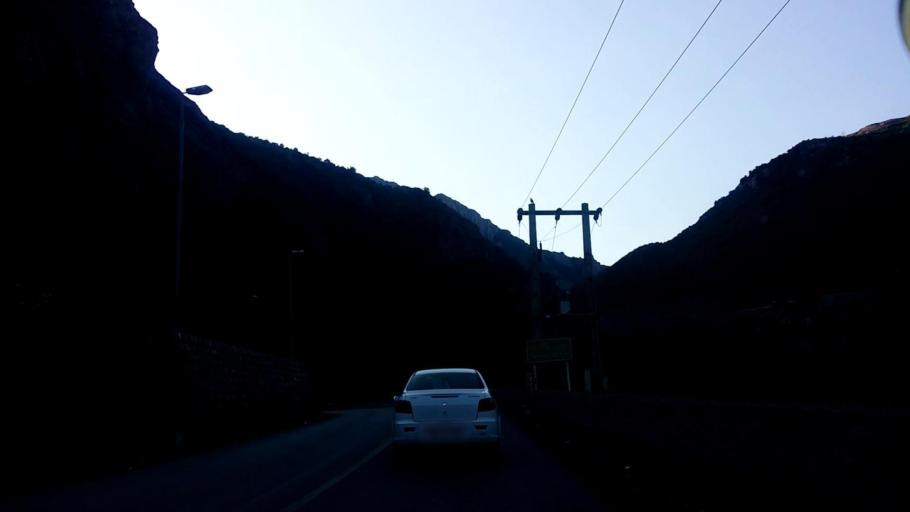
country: IR
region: Tehran
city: Tajrish
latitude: 36.2169
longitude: 51.3147
